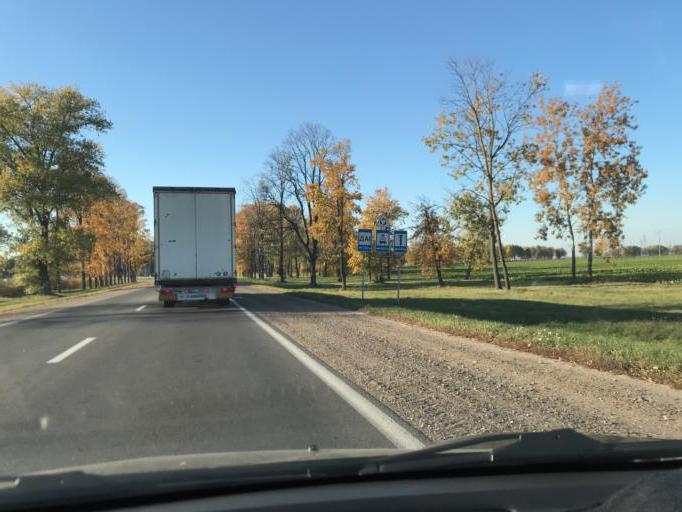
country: BY
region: Minsk
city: Slutsk
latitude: 53.0512
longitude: 27.5577
